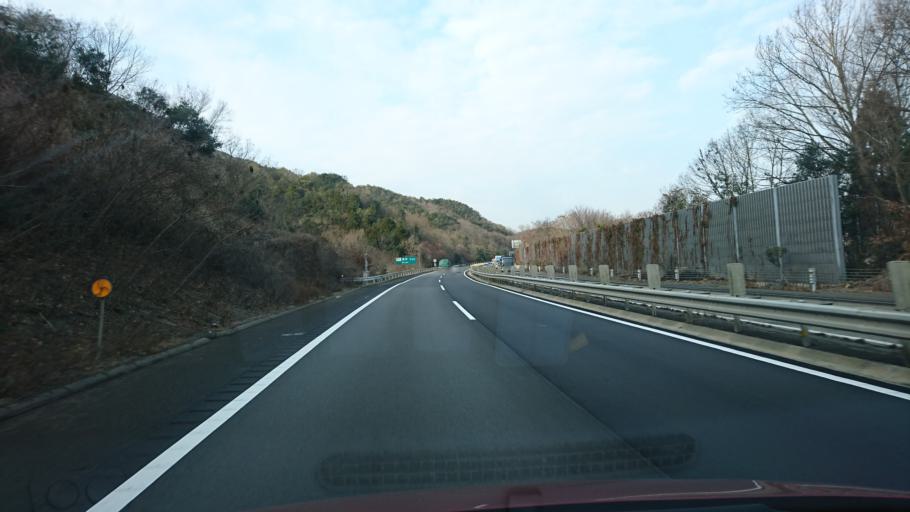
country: JP
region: Hyogo
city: Kariya
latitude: 34.7816
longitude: 134.2894
